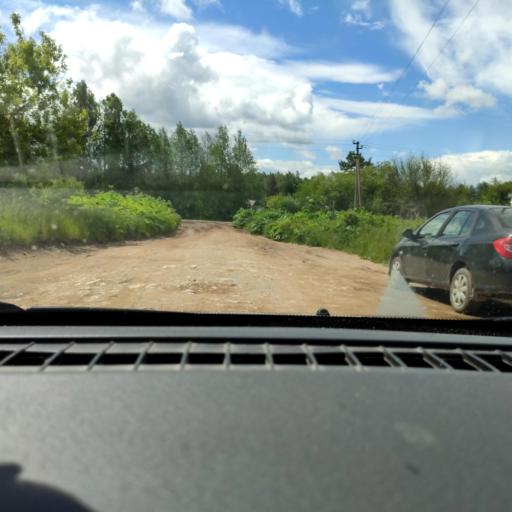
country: RU
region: Perm
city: Overyata
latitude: 58.1239
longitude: 55.8110
